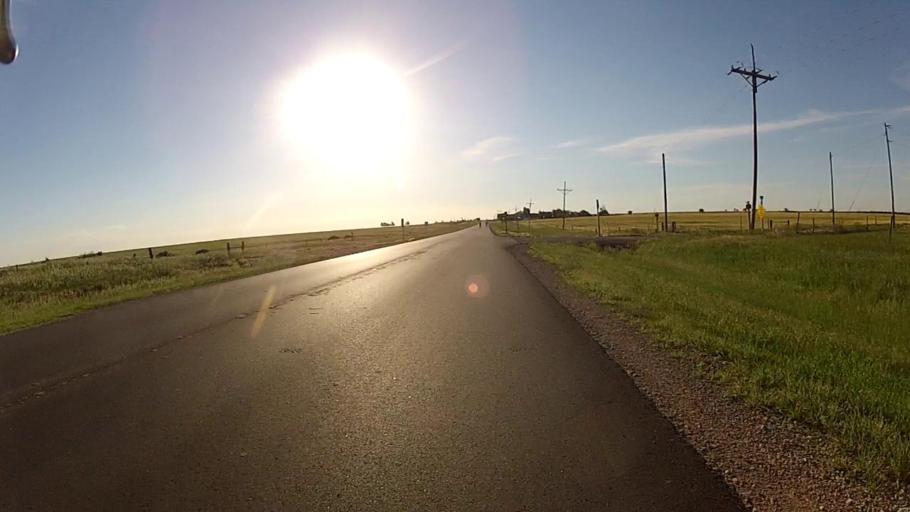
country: US
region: Kansas
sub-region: Comanche County
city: Coldwater
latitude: 37.2820
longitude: -99.1509
